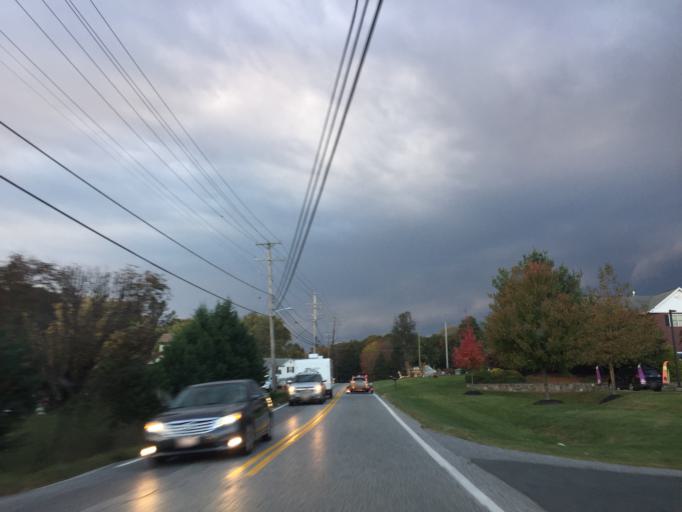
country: US
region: Maryland
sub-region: Baltimore County
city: White Marsh
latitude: 39.3756
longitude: -76.4171
